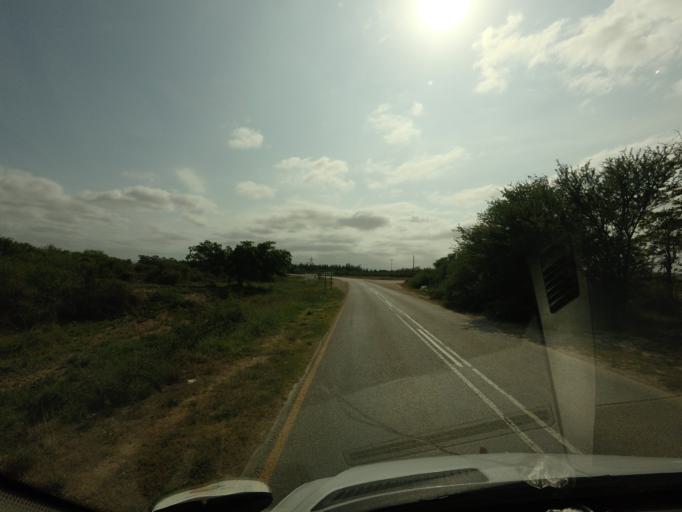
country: ZA
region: Eastern Cape
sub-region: Cacadu District Municipality
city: Kirkwood
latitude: -33.5813
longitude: 25.6745
